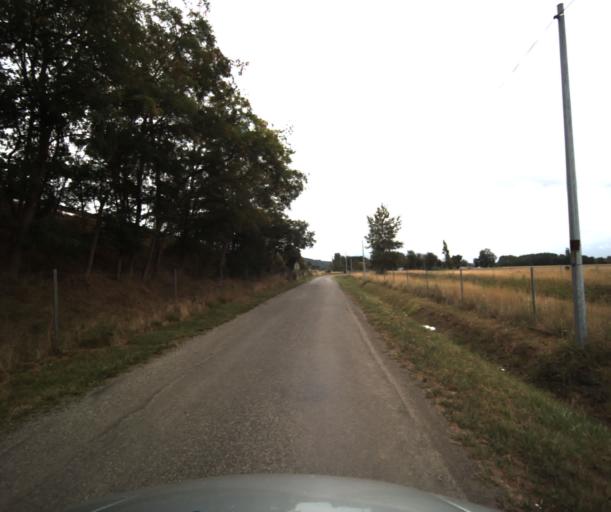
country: FR
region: Midi-Pyrenees
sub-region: Departement de la Haute-Garonne
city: Le Fauga
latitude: 43.4420
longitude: 1.3078
